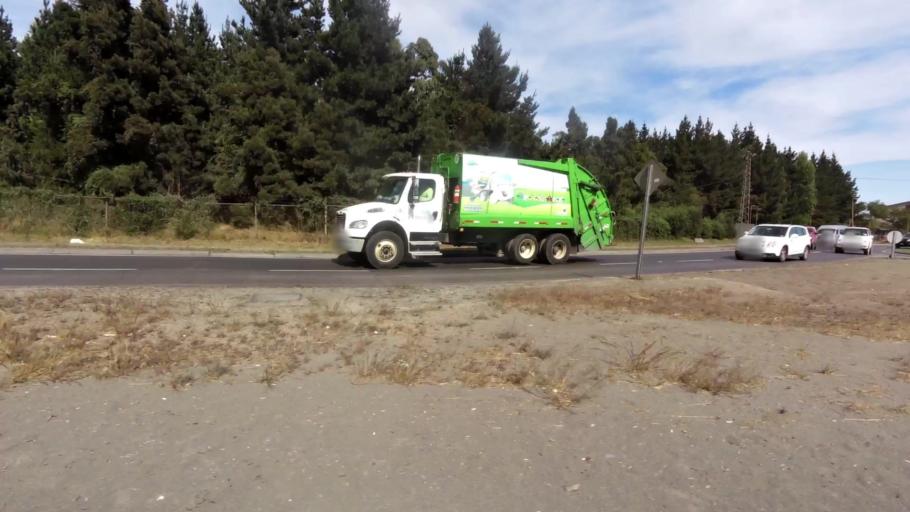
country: CL
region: Biobio
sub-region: Provincia de Concepcion
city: Talcahuano
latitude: -36.7530
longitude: -73.1239
